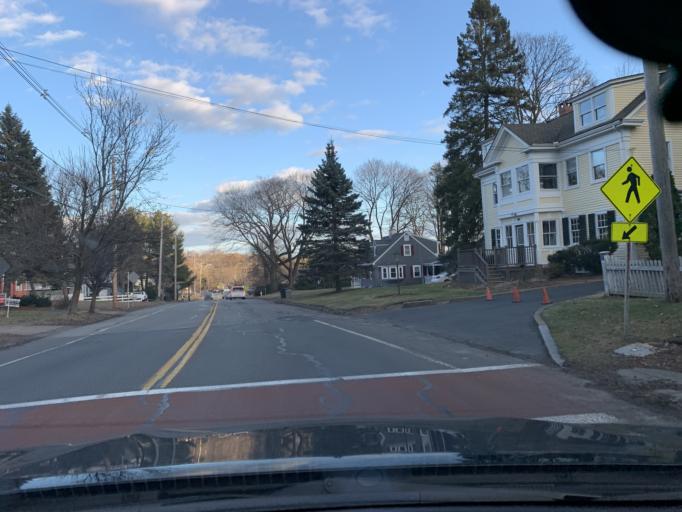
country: US
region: Massachusetts
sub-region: Essex County
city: Danvers
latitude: 42.5723
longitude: -70.9516
